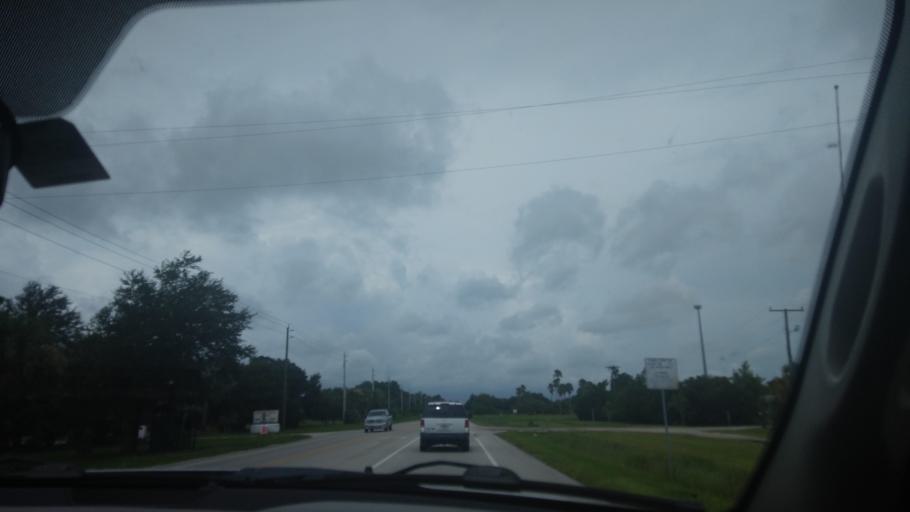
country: US
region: Florida
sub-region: Indian River County
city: Fellsmere
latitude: 27.7677
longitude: -80.5771
